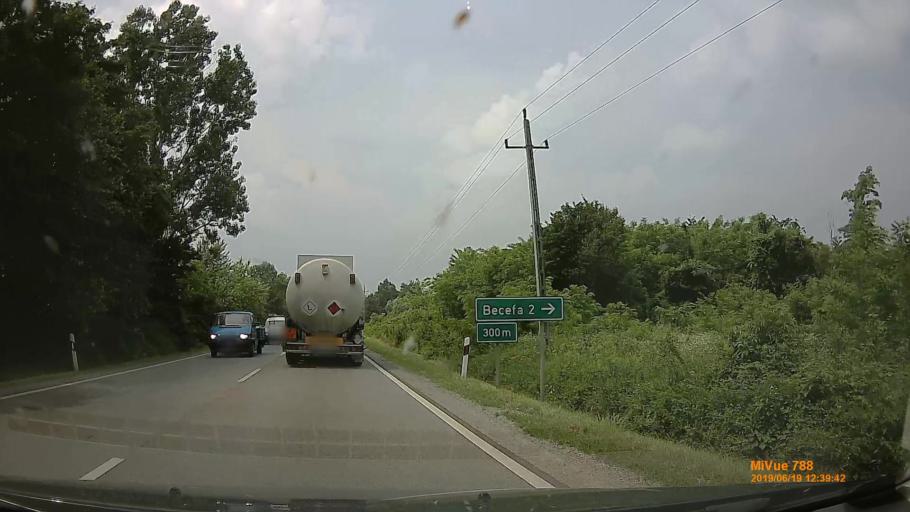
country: HU
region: Baranya
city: Szigetvar
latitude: 46.0485
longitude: 17.8516
